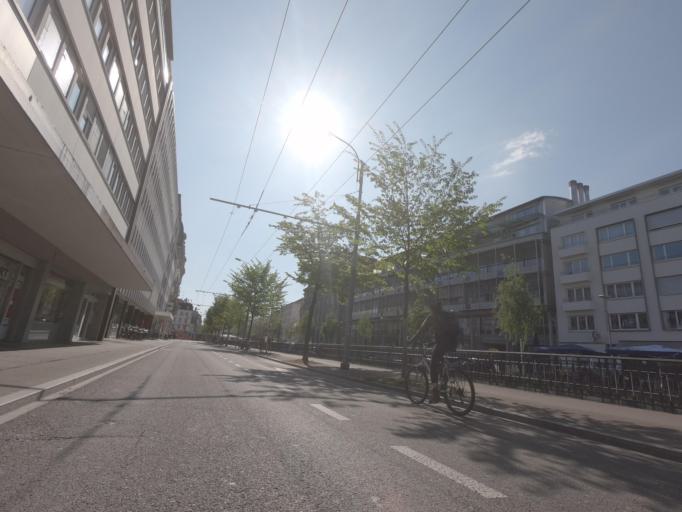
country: CH
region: Bern
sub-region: Biel/Bienne District
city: Biel/Bienne
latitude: 47.1376
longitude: 7.2483
